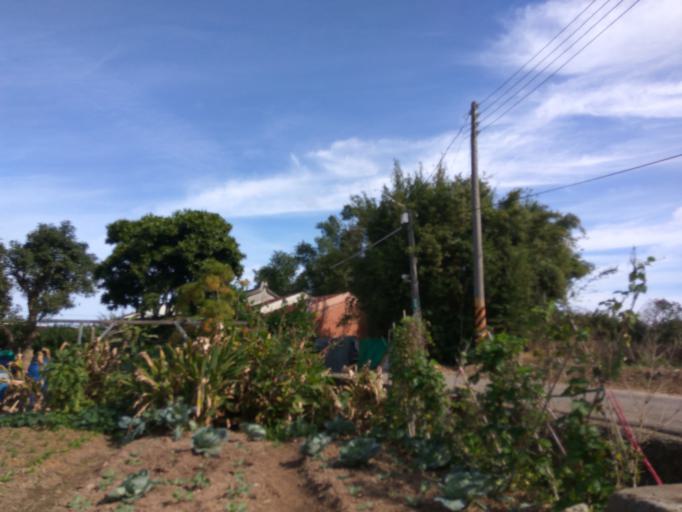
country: TW
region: Taiwan
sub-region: Hsinchu
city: Zhubei
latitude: 25.0139
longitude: 121.0770
